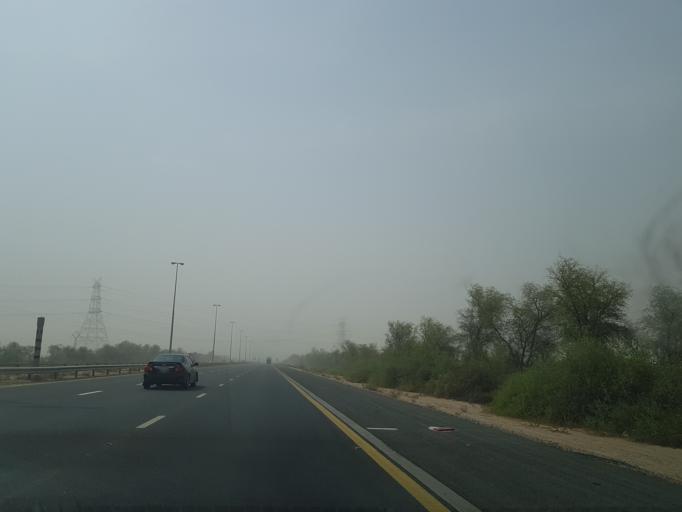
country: AE
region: Dubai
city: Dubai
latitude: 24.9309
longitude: 55.5169
